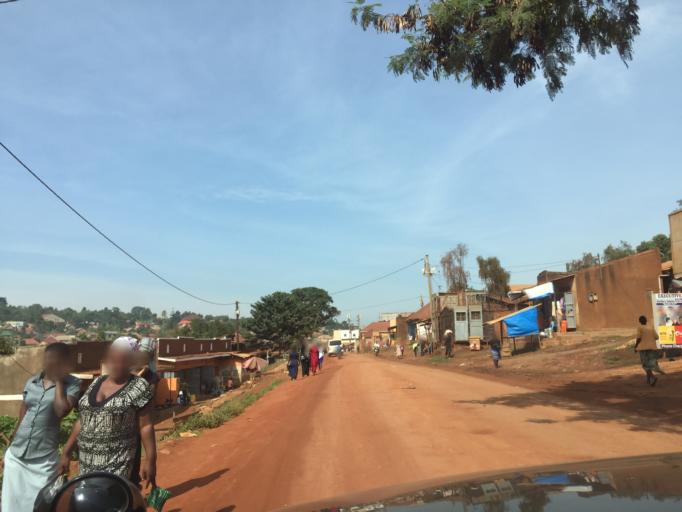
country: UG
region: Central Region
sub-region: Wakiso District
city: Wakiso
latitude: 0.4609
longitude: 32.5314
